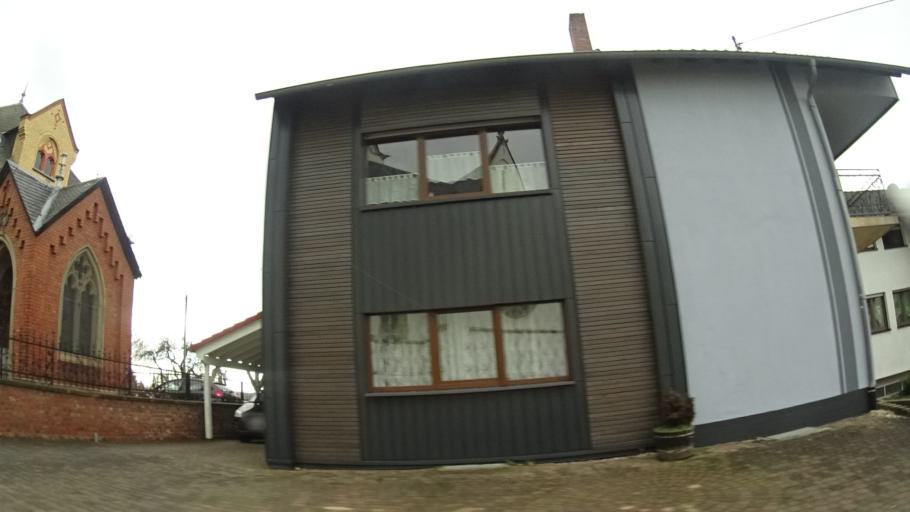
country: DE
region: Rheinland-Pfalz
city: Daxweiler
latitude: 49.9656
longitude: 7.7519
